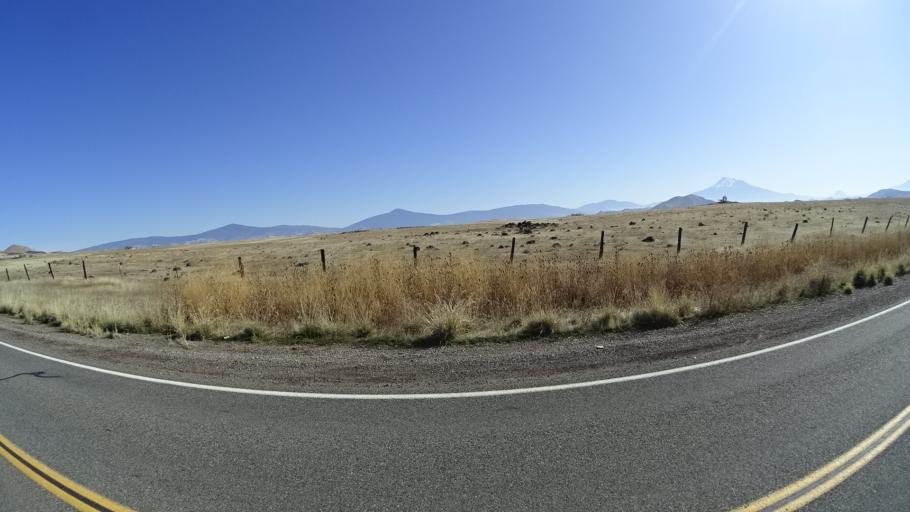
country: US
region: California
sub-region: Siskiyou County
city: Montague
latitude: 41.7595
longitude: -122.5749
